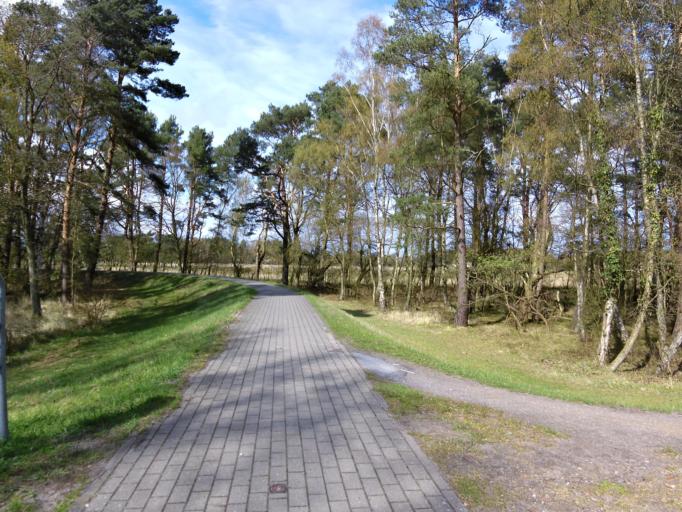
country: DE
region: Mecklenburg-Vorpommern
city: Zingst
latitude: 54.4357
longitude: 12.6651
